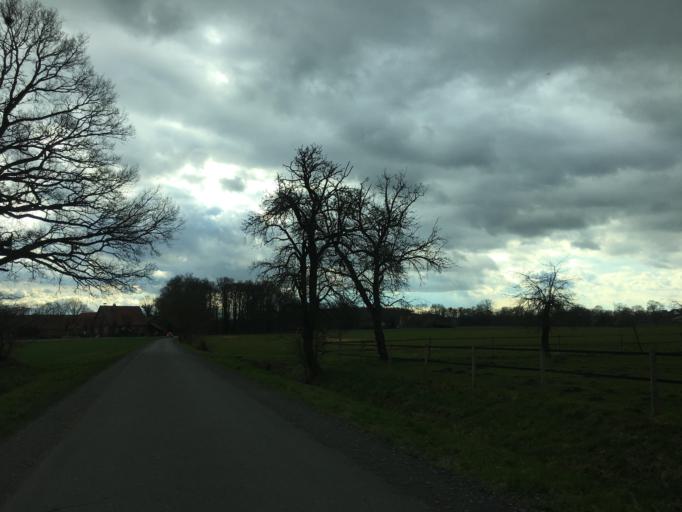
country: DE
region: North Rhine-Westphalia
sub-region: Regierungsbezirk Munster
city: Muenster
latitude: 52.0166
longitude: 7.6374
